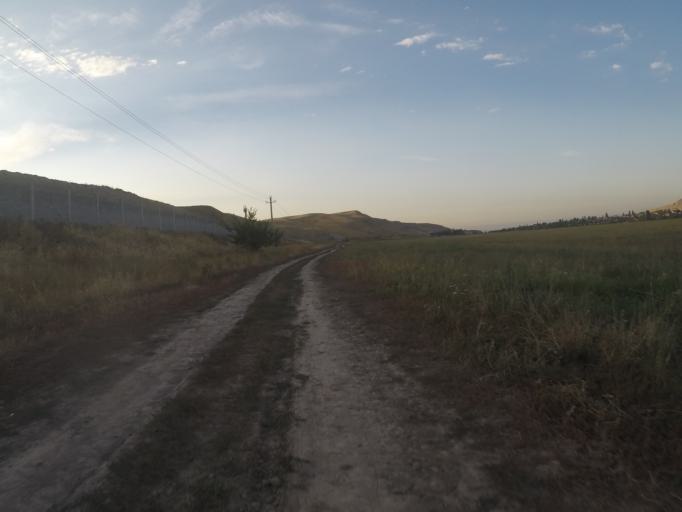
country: KG
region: Chuy
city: Bishkek
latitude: 42.7552
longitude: 74.6364
